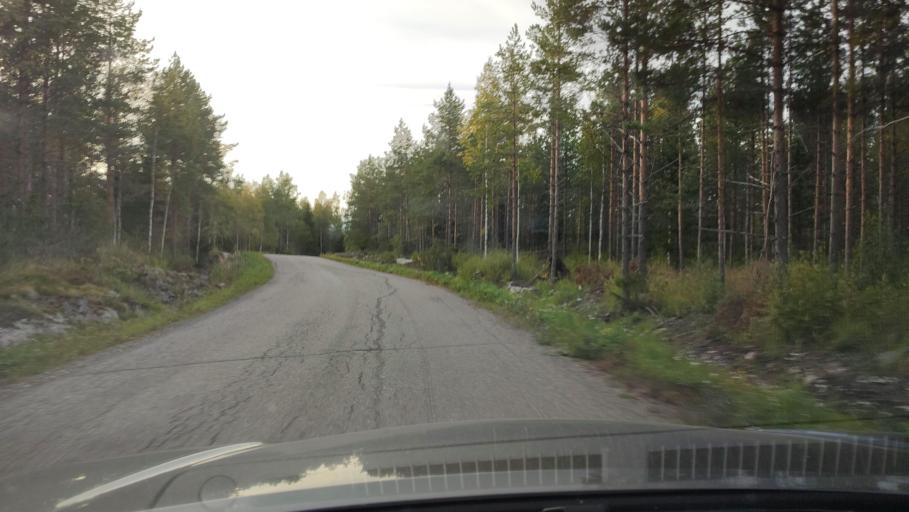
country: FI
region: Ostrobothnia
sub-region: Sydosterbotten
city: Kristinestad
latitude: 62.1504
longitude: 21.5490
